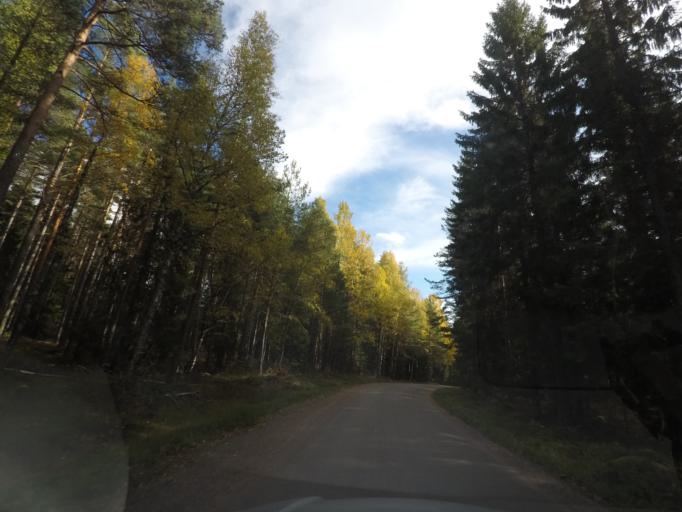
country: SE
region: Vaestmanland
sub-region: Kungsors Kommun
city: Kungsoer
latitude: 59.3345
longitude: 16.2181
